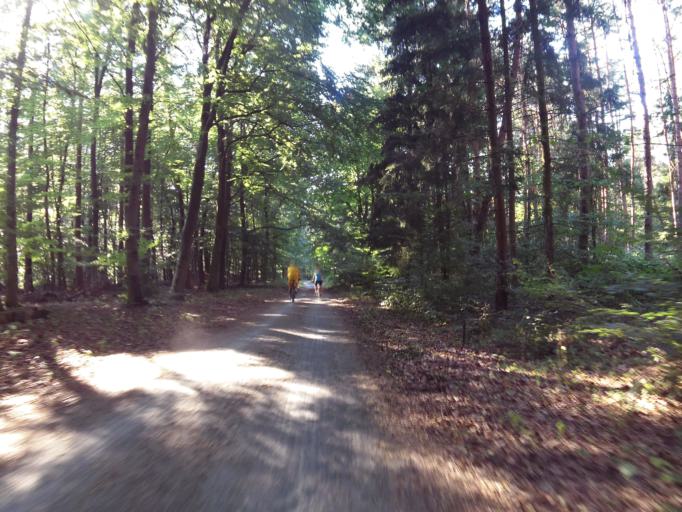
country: DE
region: Hesse
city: Morfelden-Walldorf
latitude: 49.9685
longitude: 8.5260
